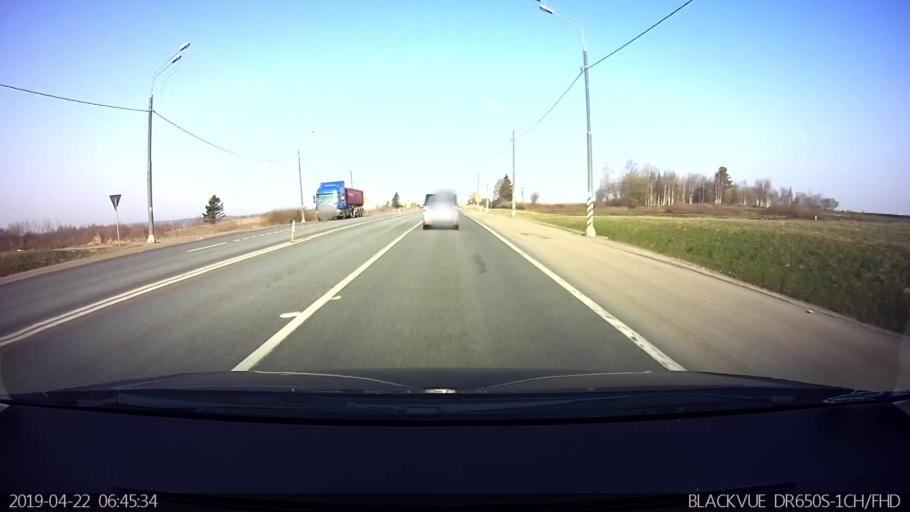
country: RU
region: Smolensk
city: Gagarin
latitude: 55.5048
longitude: 35.1317
